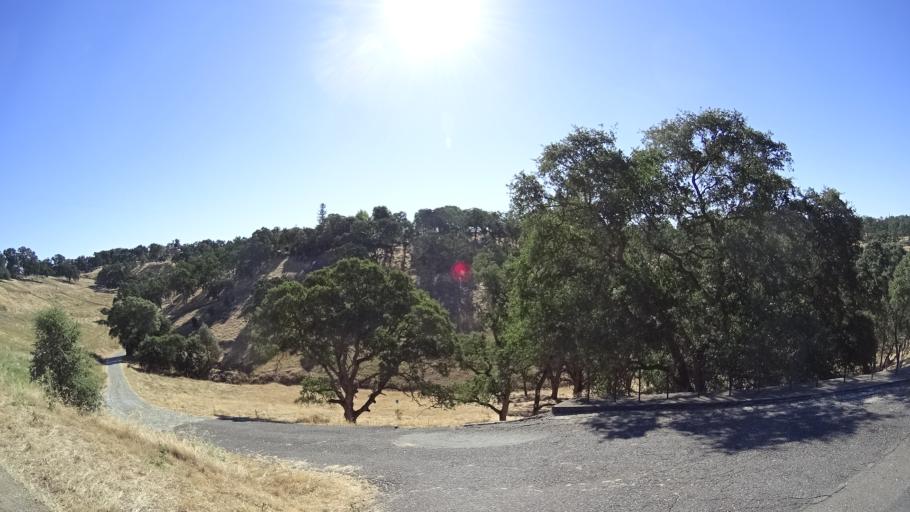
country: US
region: California
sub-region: Calaveras County
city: Rancho Calaveras
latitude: 38.1185
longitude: -120.8727
